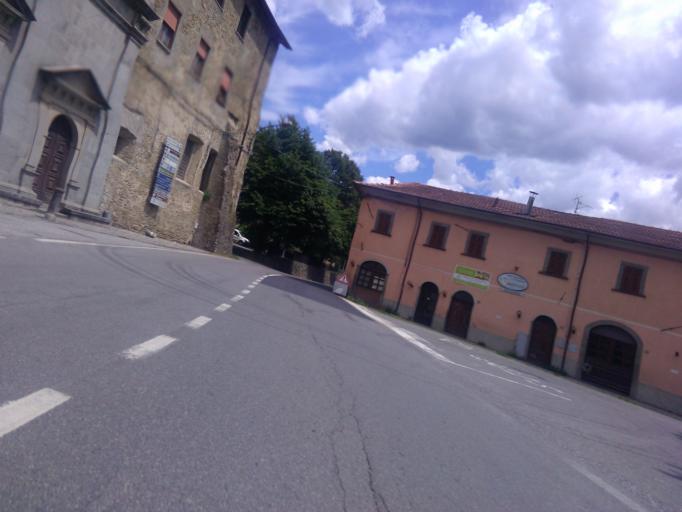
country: IT
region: Tuscany
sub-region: Provincia di Massa-Carrara
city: Pontremoli
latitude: 44.3636
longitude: 9.8882
